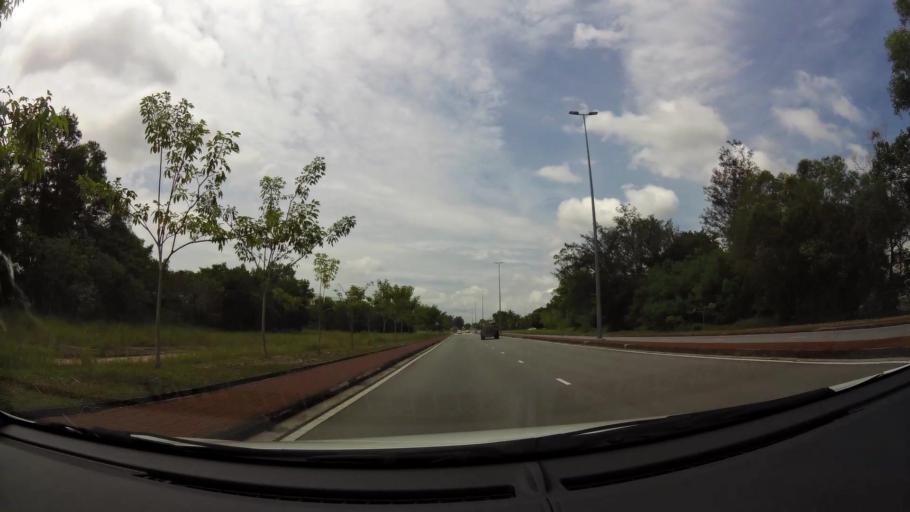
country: BN
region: Brunei and Muara
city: Bandar Seri Begawan
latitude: 4.9183
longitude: 114.9269
